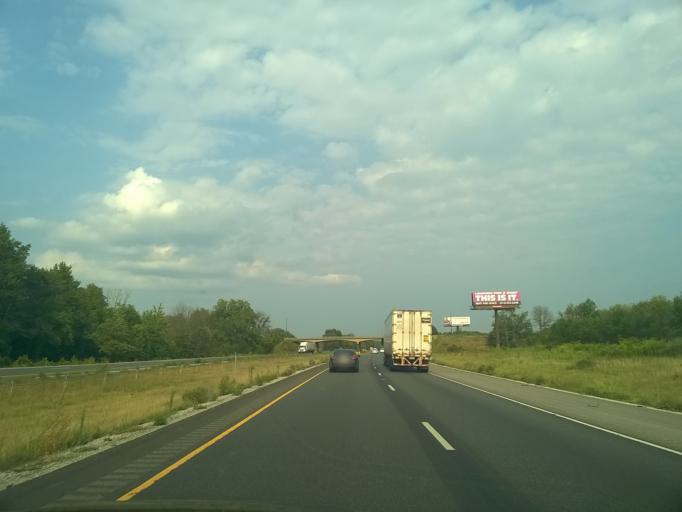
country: US
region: Indiana
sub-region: Clay County
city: Brazil
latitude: 39.4631
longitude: -87.0727
